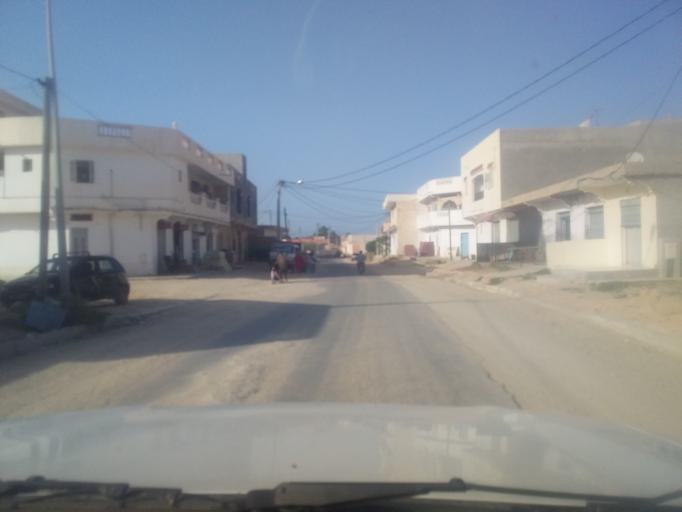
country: TN
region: Qabis
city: Matmata
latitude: 33.6130
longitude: 10.2846
